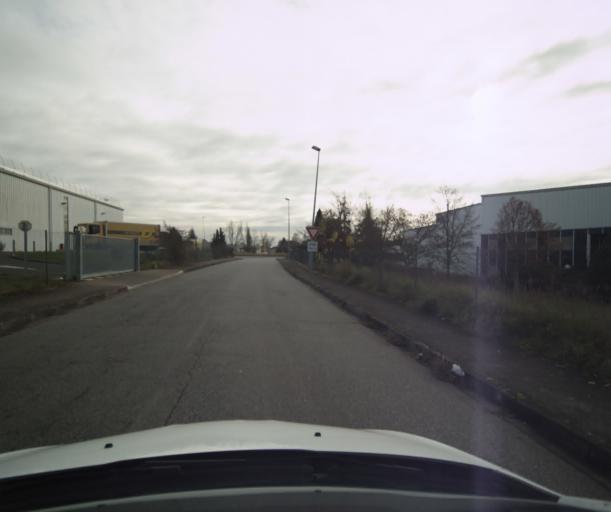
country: FR
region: Midi-Pyrenees
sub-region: Departement de la Haute-Garonne
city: Lespinasse
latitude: 43.7203
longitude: 1.3920
